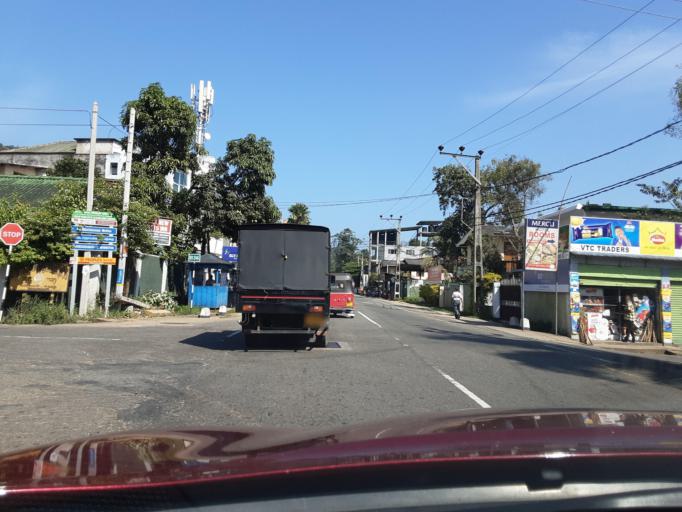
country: LK
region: Uva
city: Badulla
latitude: 6.9970
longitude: 81.0573
